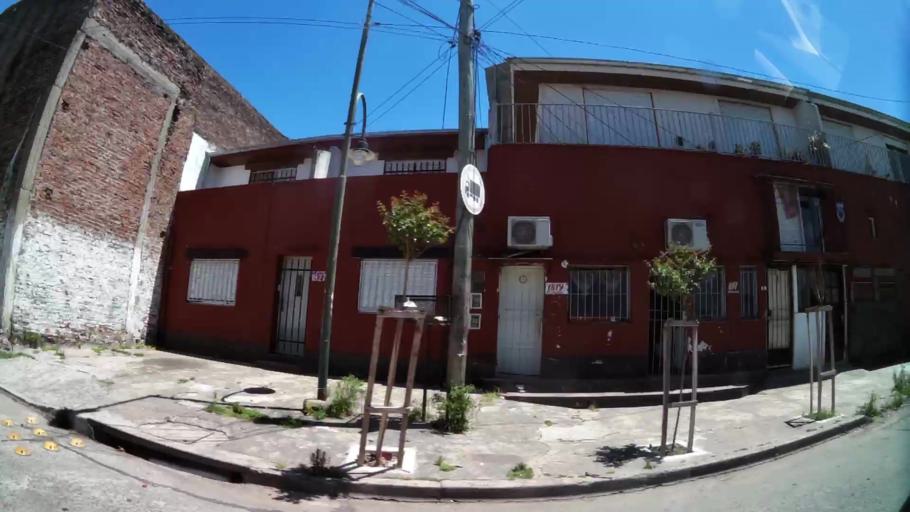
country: AR
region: Buenos Aires
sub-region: Partido de Tigre
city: Tigre
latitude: -34.4484
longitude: -58.5574
